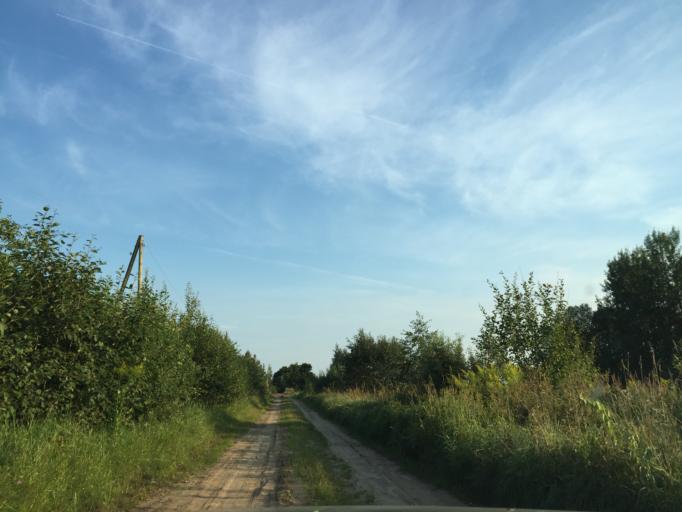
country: LV
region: Limbazu Rajons
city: Limbazi
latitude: 57.5637
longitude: 24.7734
